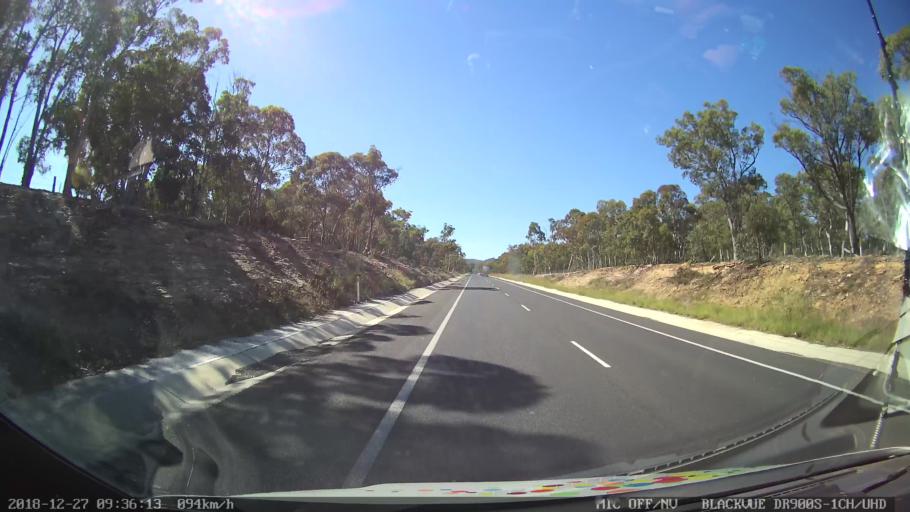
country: AU
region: New South Wales
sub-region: Lithgow
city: Portland
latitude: -33.2492
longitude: 150.0339
